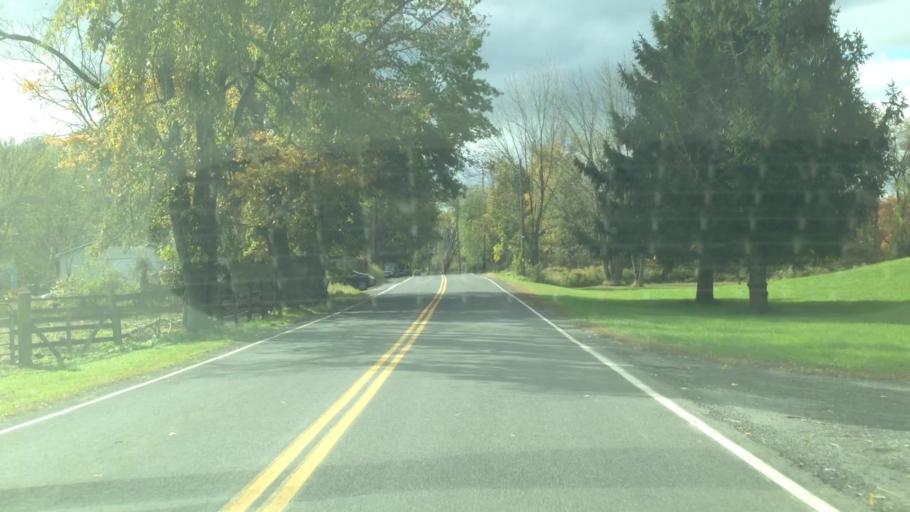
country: US
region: New York
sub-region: Ulster County
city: New Paltz
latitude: 41.7781
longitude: -74.0898
